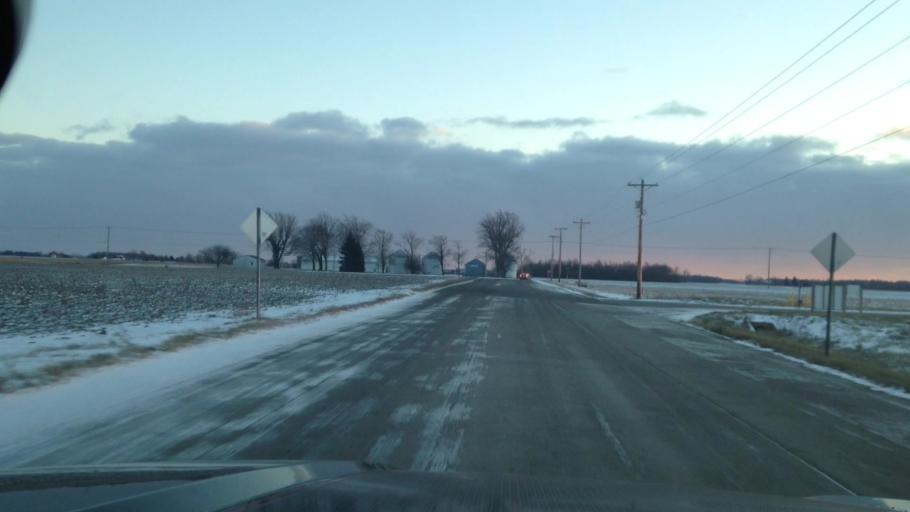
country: US
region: Indiana
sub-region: Randolph County
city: Union City
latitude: 40.1806
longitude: -84.8624
